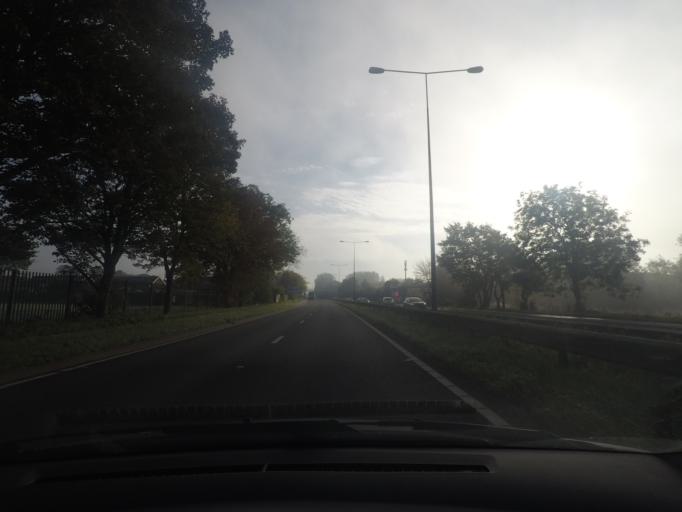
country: GB
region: England
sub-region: East Riding of Yorkshire
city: Welton
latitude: 53.7261
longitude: -0.5345
